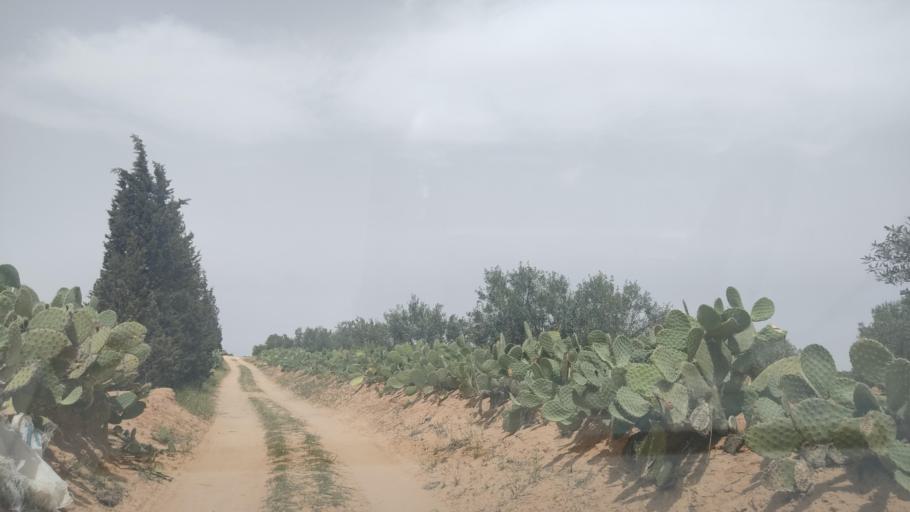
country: TN
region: Safaqis
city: Sfax
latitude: 34.8410
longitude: 10.5939
